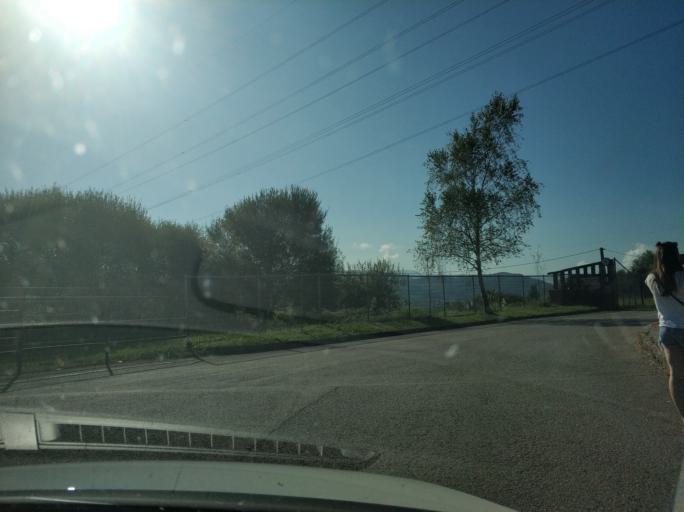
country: ES
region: Cantabria
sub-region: Provincia de Cantabria
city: Penagos
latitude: 43.3500
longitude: -3.8426
